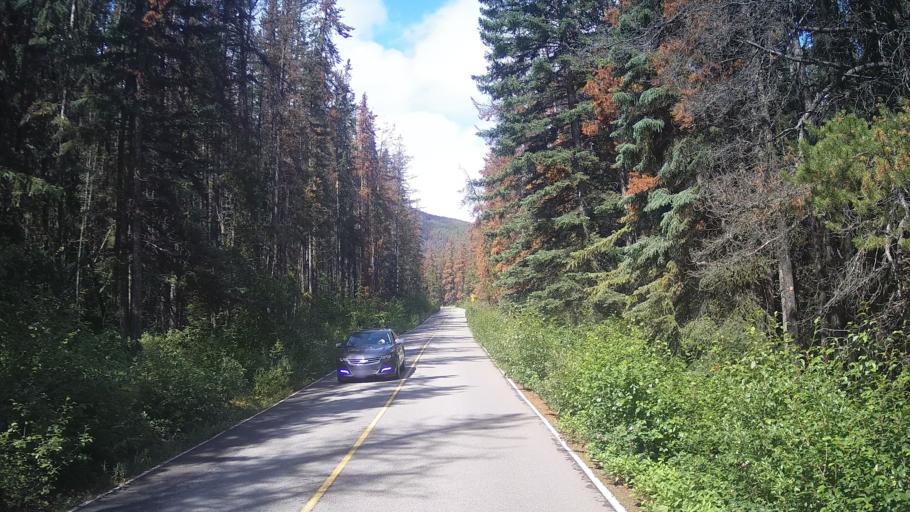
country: CA
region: Alberta
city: Jasper Park Lodge
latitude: 52.7699
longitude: -118.0331
